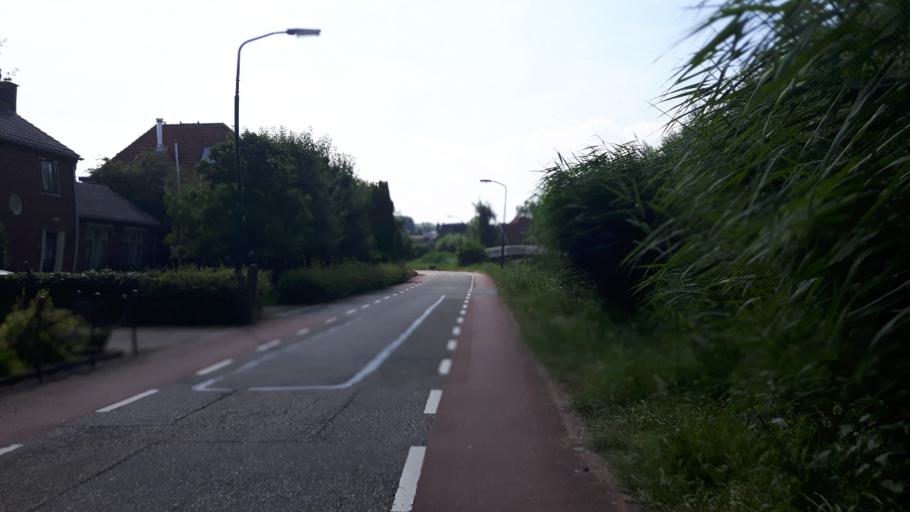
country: NL
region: Utrecht
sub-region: Gemeente Woerden
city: Woerden
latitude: 52.0630
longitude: 4.9123
